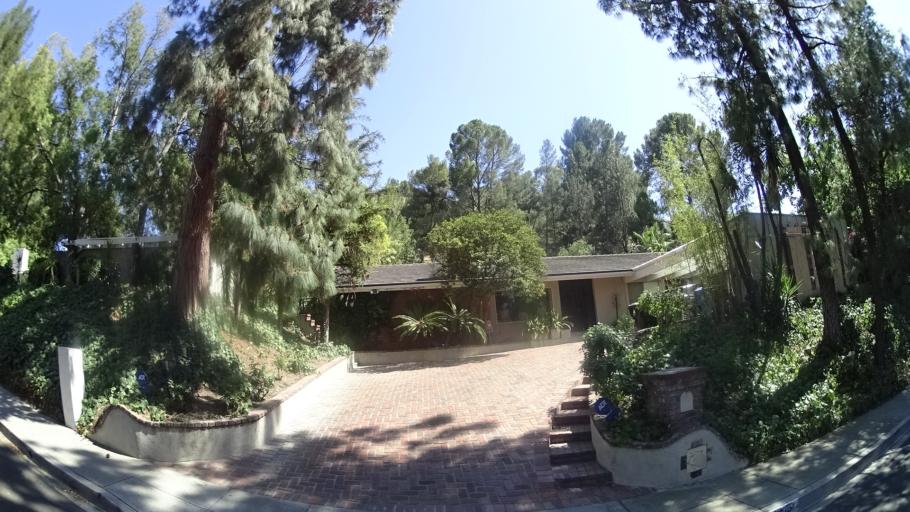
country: US
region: California
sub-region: Los Angeles County
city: Sherman Oaks
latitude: 34.1336
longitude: -118.4867
